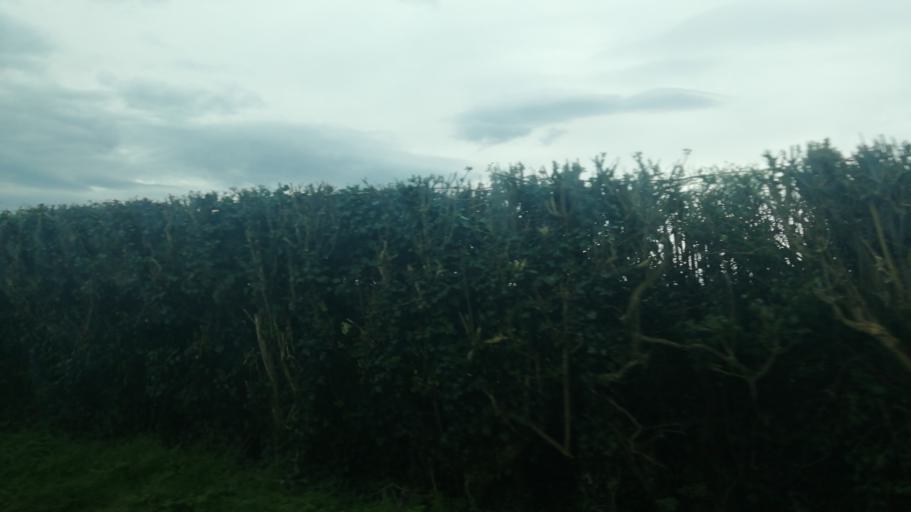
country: IE
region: Leinster
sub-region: Kildare
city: Clane
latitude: 53.3053
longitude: -6.7098
